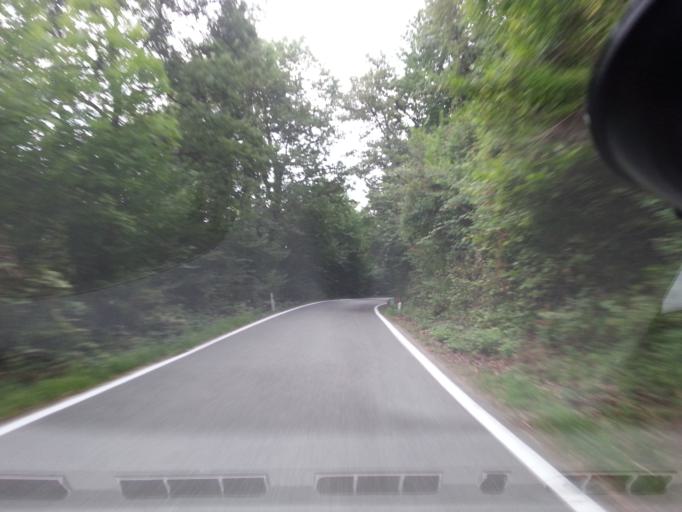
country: IT
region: Piedmont
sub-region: Provincia di Torino
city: Valgioie
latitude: 45.0721
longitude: 7.3621
